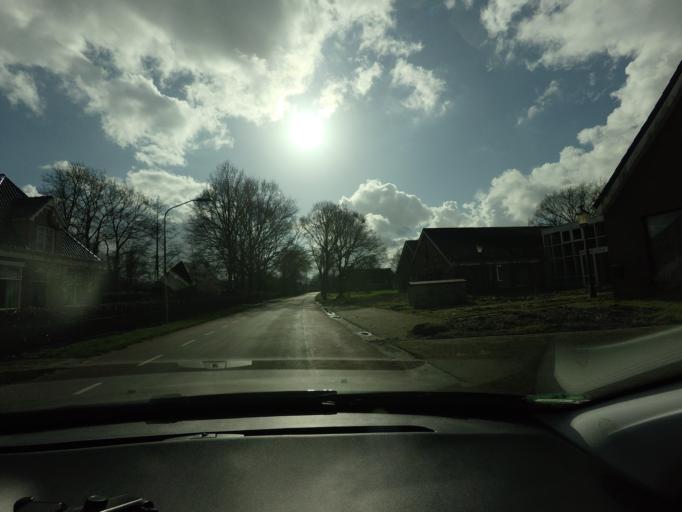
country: NL
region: Drenthe
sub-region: Gemeente Assen
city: Assen
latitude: 52.8725
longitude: 6.5876
